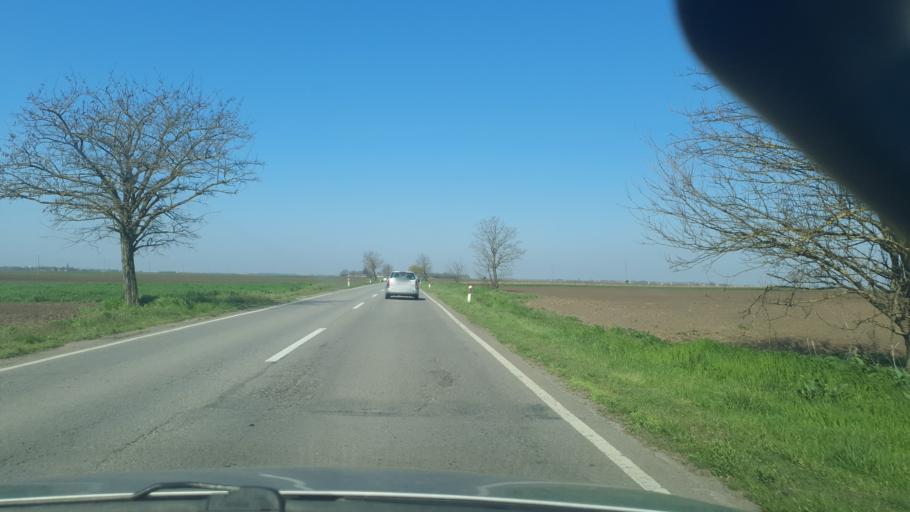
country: RS
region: Autonomna Pokrajina Vojvodina
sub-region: Zapadnobacki Okrug
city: Sombor
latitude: 45.7679
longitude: 19.2305
